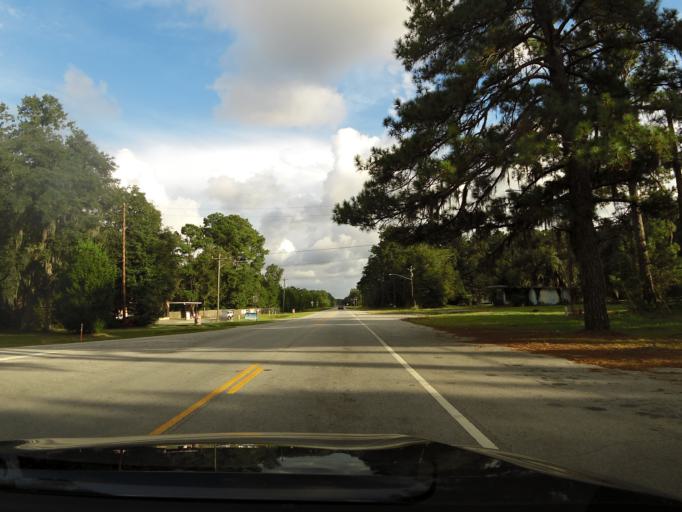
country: US
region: Georgia
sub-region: Liberty County
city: Midway
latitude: 31.7321
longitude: -81.4295
